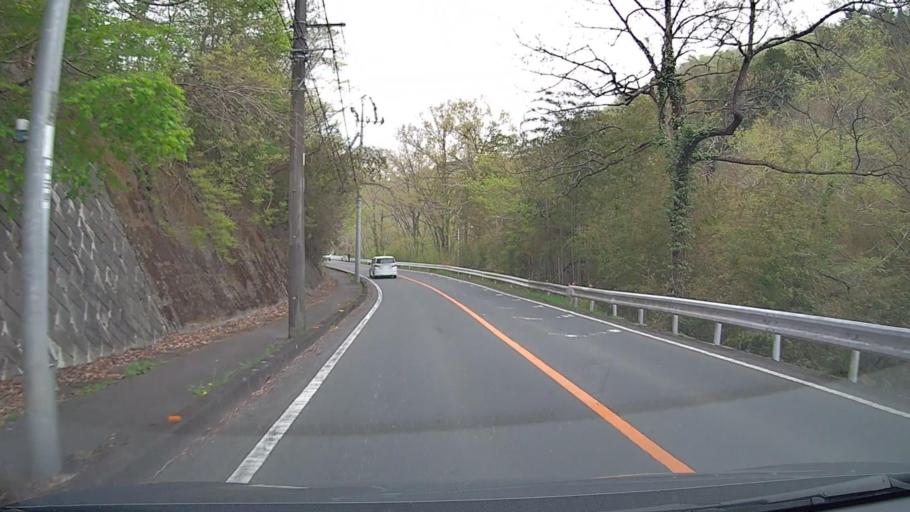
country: JP
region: Saitama
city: Yorii
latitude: 36.0707
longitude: 139.1208
